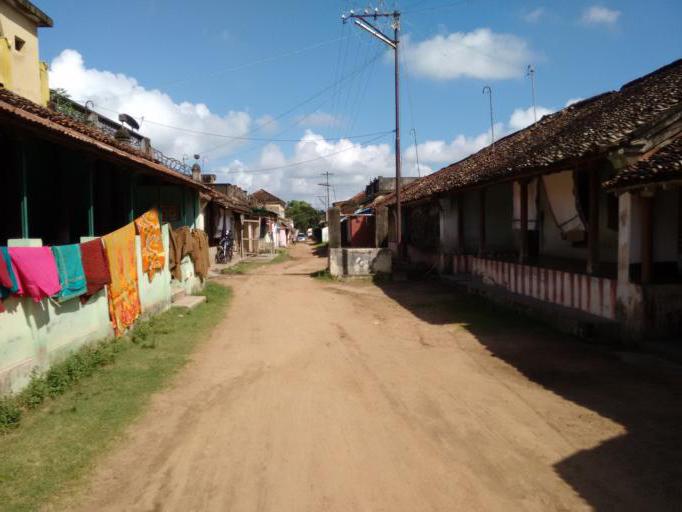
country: IN
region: Tamil Nadu
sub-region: Thiruvarur
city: Koradachcheri
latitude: 10.8504
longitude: 79.5122
